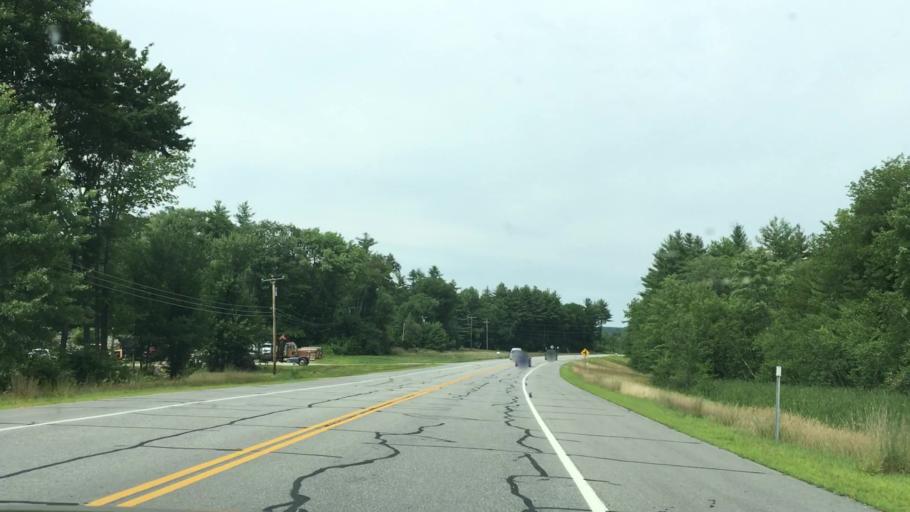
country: US
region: New Hampshire
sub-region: Hillsborough County
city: Antrim
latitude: 43.0452
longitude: -71.9322
